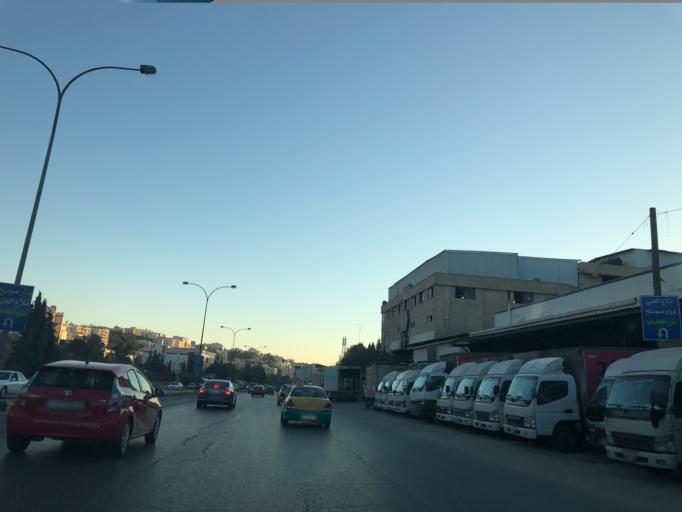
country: JO
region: Amman
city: Al Jubayhah
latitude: 32.0128
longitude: 35.8417
